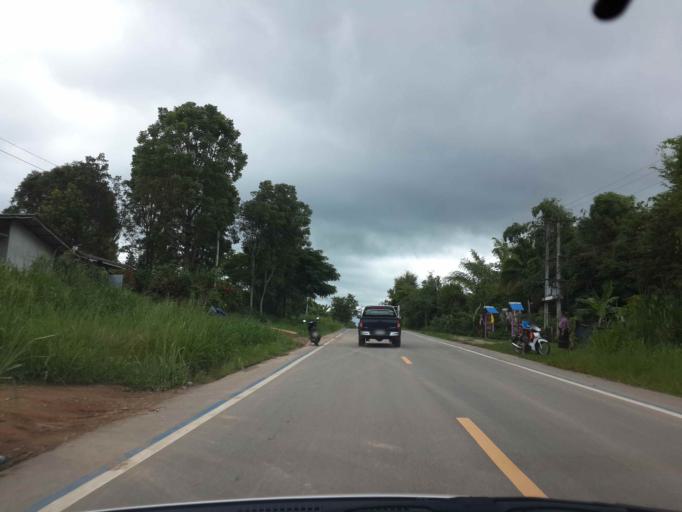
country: TH
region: Ratchaburi
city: Suan Phueng
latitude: 13.6480
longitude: 99.2118
